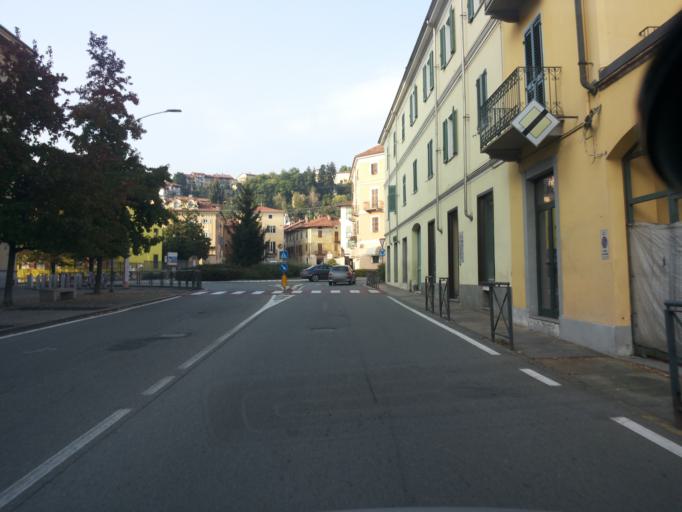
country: IT
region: Piedmont
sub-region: Provincia di Biella
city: Biella
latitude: 45.5593
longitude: 8.0478
